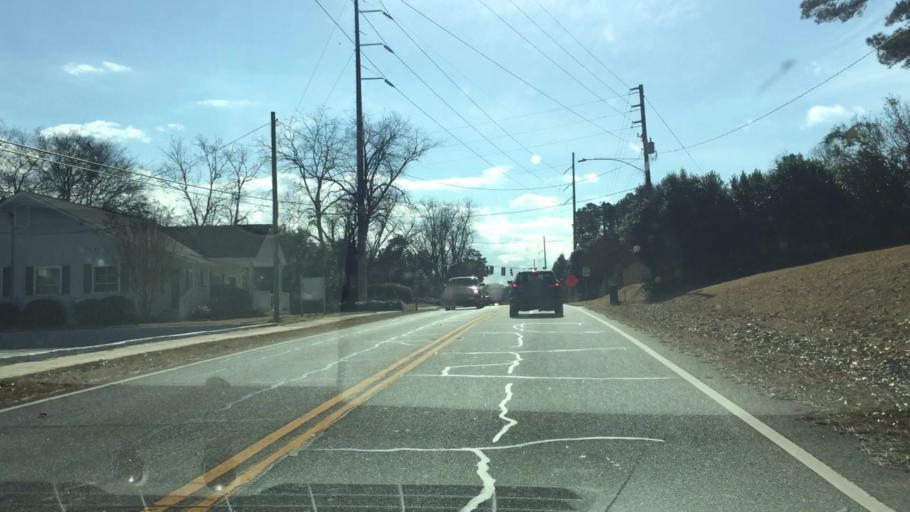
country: US
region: Georgia
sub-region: Henry County
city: McDonough
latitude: 33.4528
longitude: -84.1416
